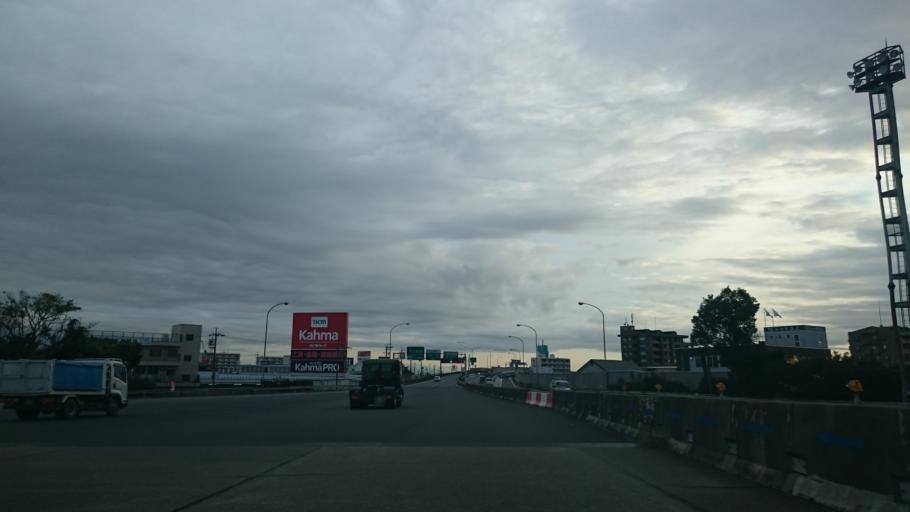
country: JP
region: Aichi
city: Kanie
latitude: 35.1536
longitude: 136.8060
